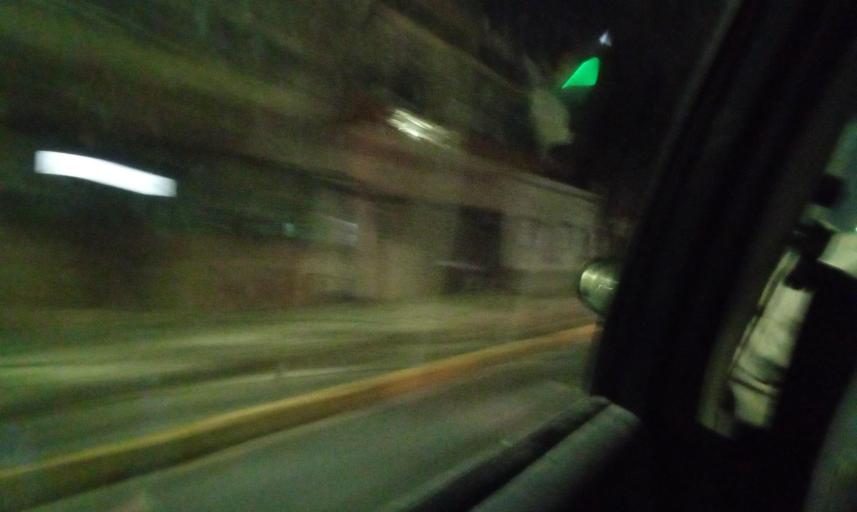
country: AR
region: Buenos Aires F.D.
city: Villa Santa Rita
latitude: -34.6165
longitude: -58.5099
